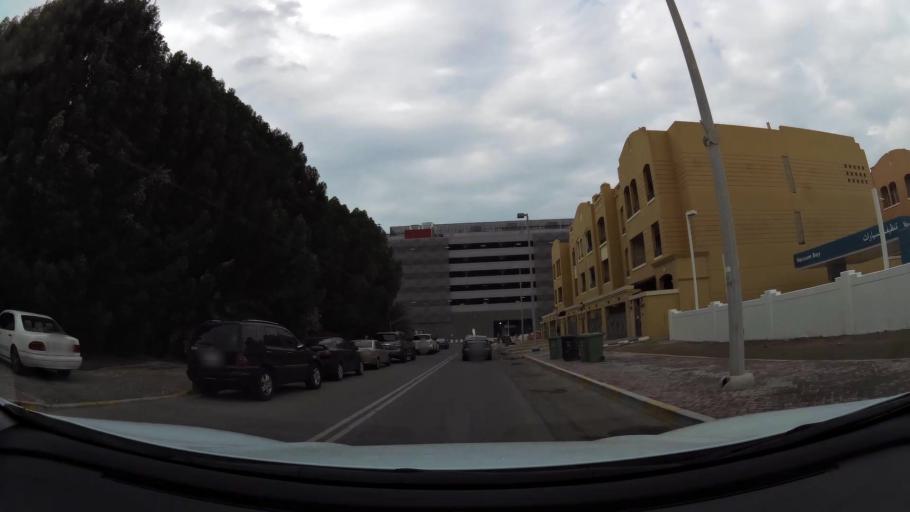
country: AE
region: Abu Dhabi
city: Abu Dhabi
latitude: 24.4480
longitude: 54.3982
